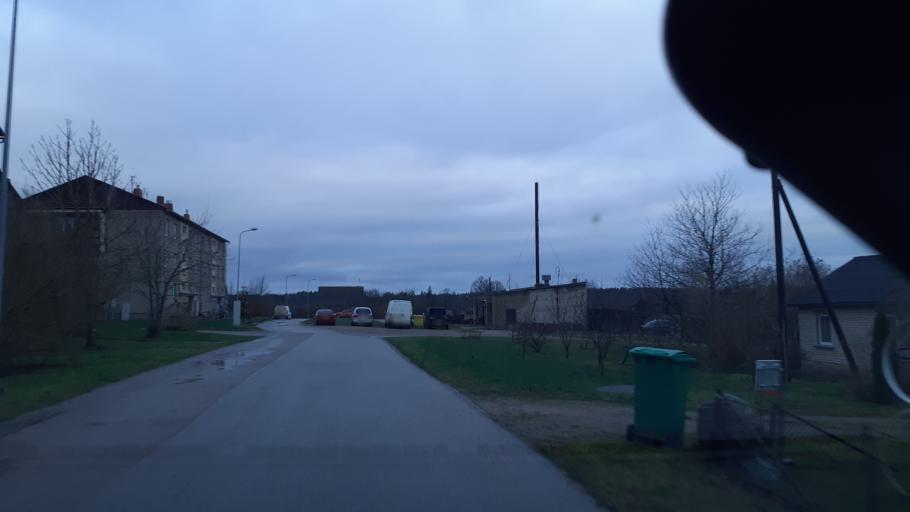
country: LV
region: Alsunga
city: Alsunga
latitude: 56.8871
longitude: 21.6033
